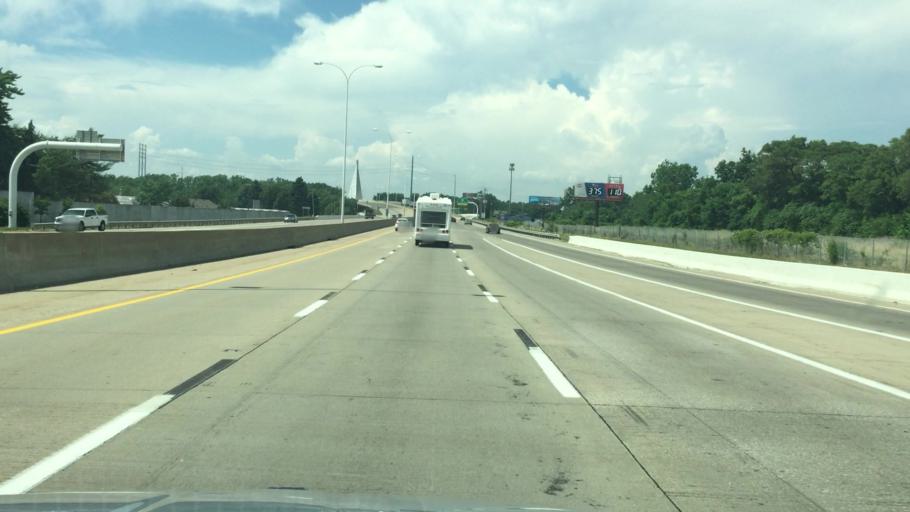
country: US
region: Ohio
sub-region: Lucas County
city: Oregon
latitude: 41.6472
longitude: -83.4996
